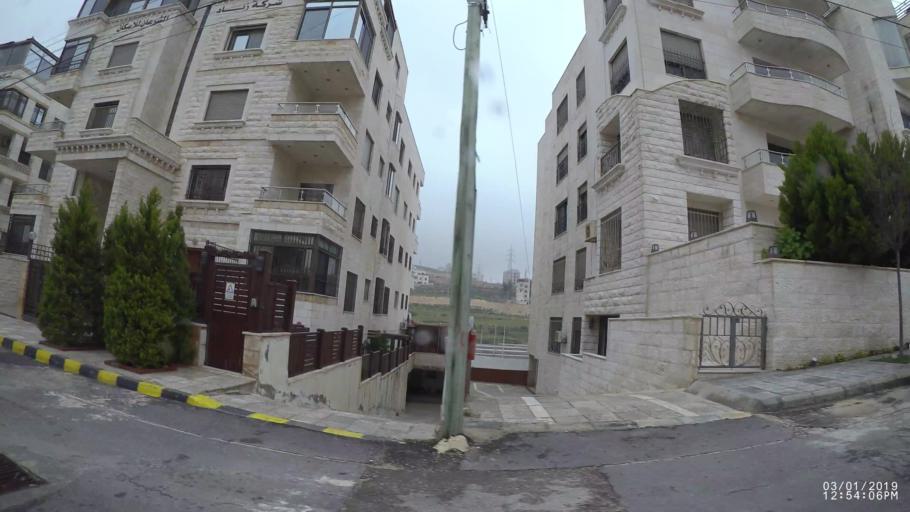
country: JO
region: Amman
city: Wadi as Sir
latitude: 31.9346
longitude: 35.8614
